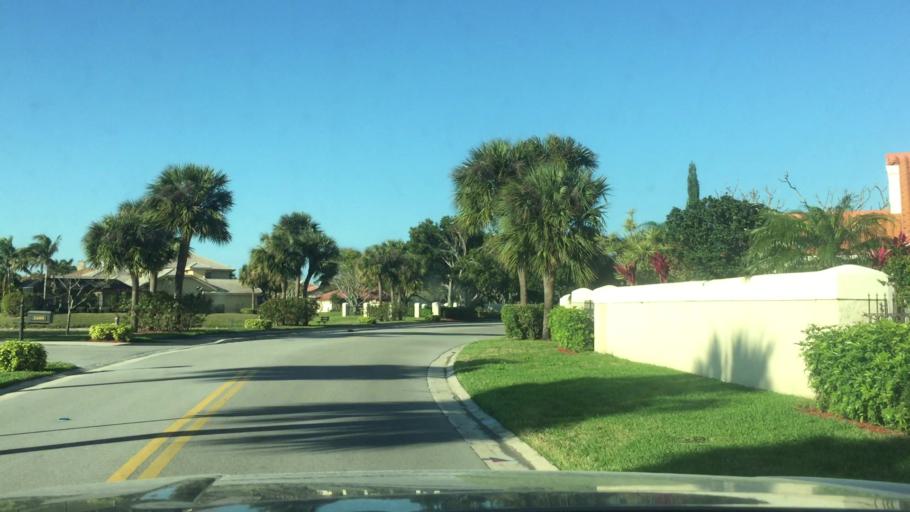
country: US
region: Florida
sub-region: Palm Beach County
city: Juno Beach
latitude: 26.8711
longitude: -80.0737
